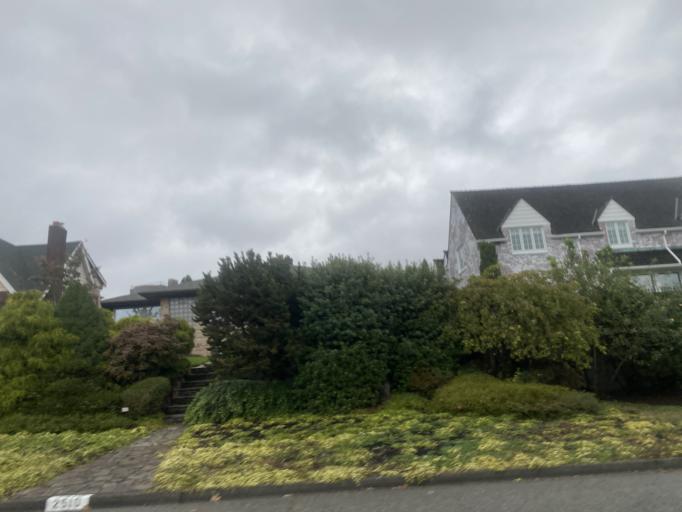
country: US
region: Washington
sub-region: King County
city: Seattle
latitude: 47.6414
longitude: -122.4133
